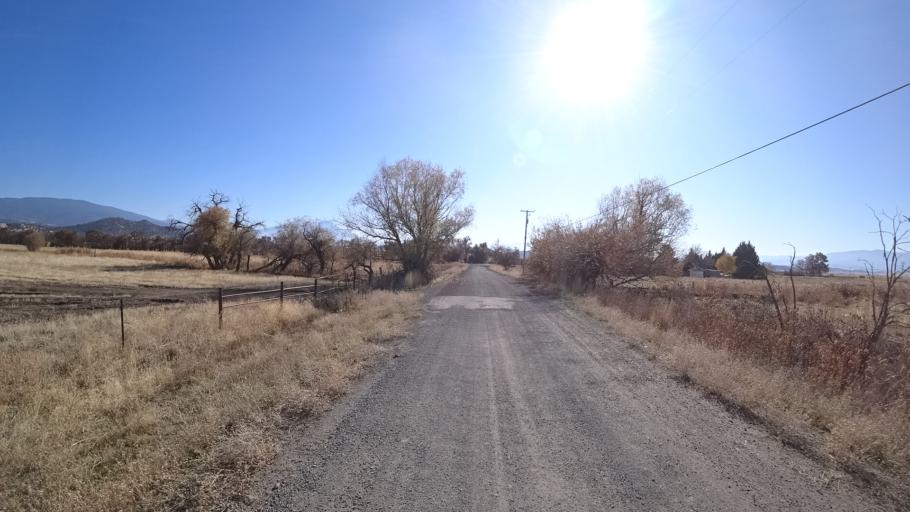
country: US
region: California
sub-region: Siskiyou County
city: Montague
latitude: 41.7278
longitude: -122.3988
